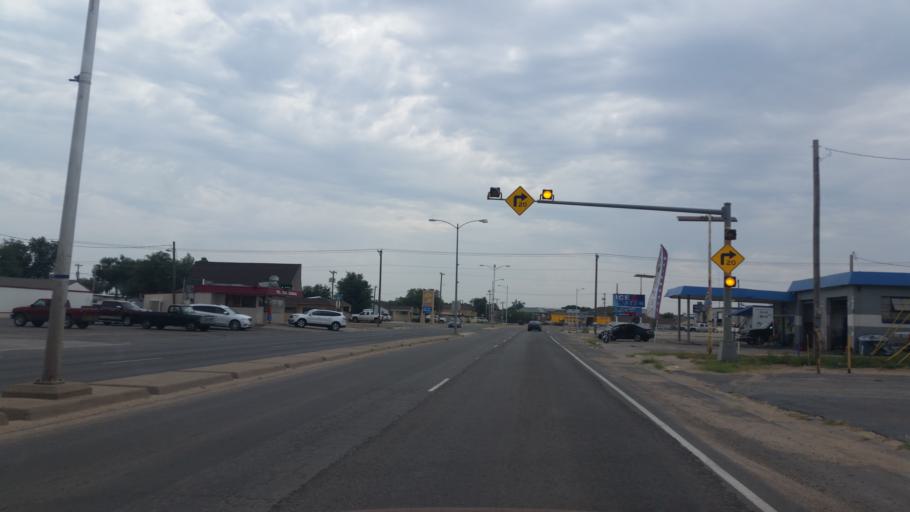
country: US
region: New Mexico
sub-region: Roosevelt County
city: Portales
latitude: 34.1889
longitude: -103.3313
